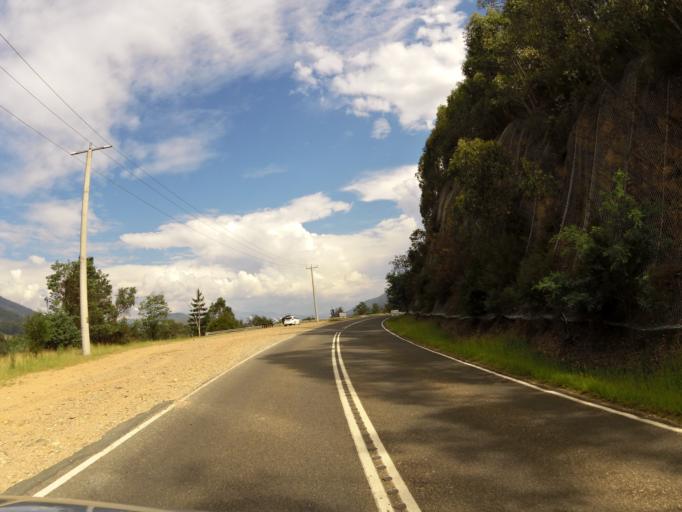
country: AU
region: Victoria
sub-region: Alpine
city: Mount Beauty
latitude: -36.7454
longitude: 147.0159
